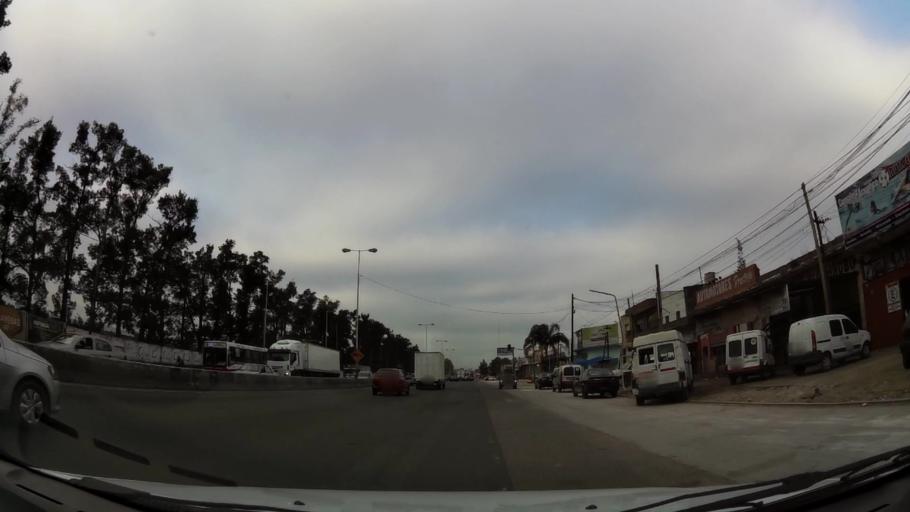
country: AR
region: Buenos Aires
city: San Justo
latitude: -34.7002
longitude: -58.5790
